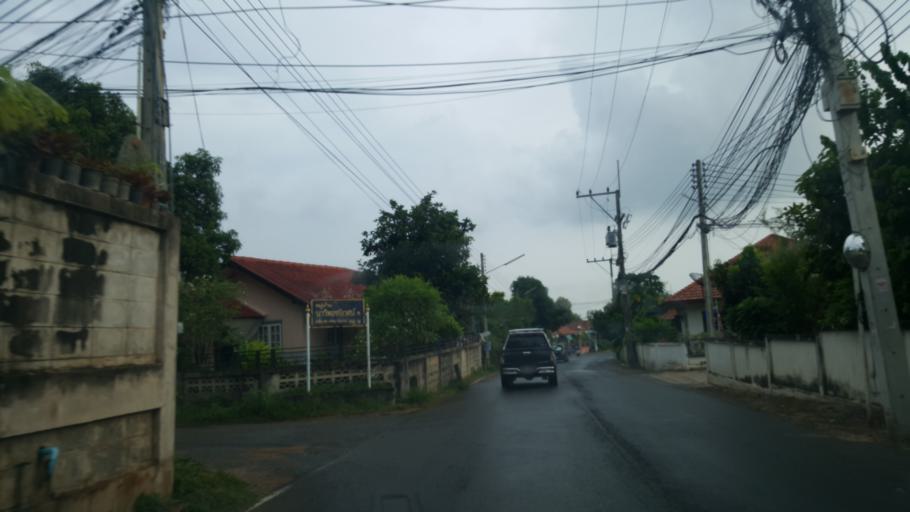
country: TH
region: Chon Buri
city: Sattahip
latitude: 12.6946
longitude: 100.9080
